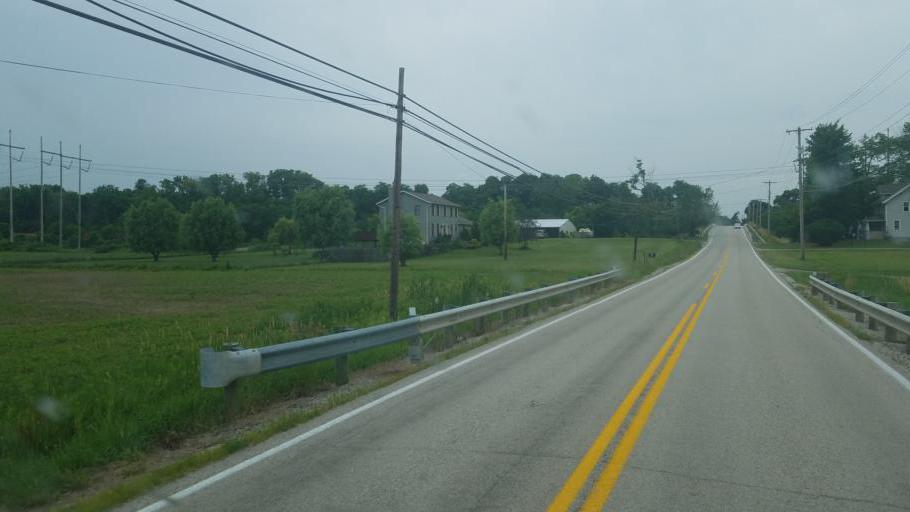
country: US
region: Ohio
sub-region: Portage County
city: Ravenna
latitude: 41.0983
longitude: -81.1997
